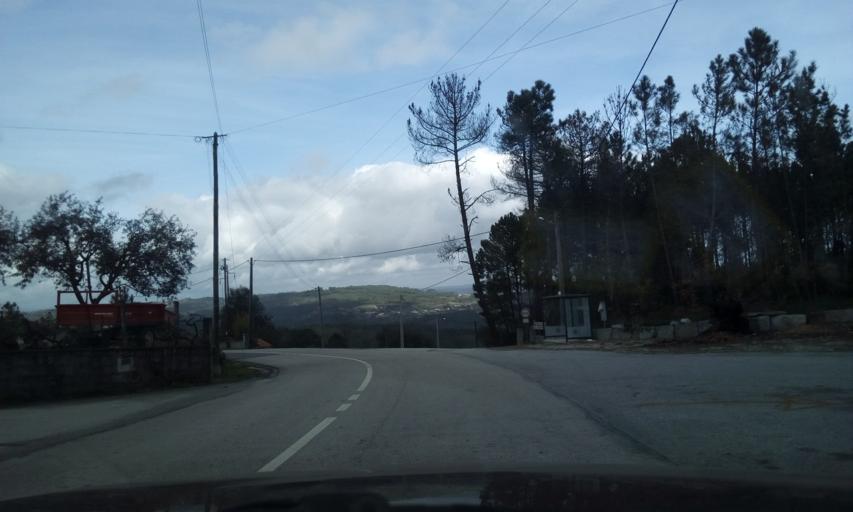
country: PT
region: Guarda
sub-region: Fornos de Algodres
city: Fornos de Algodres
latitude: 40.6630
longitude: -7.6005
